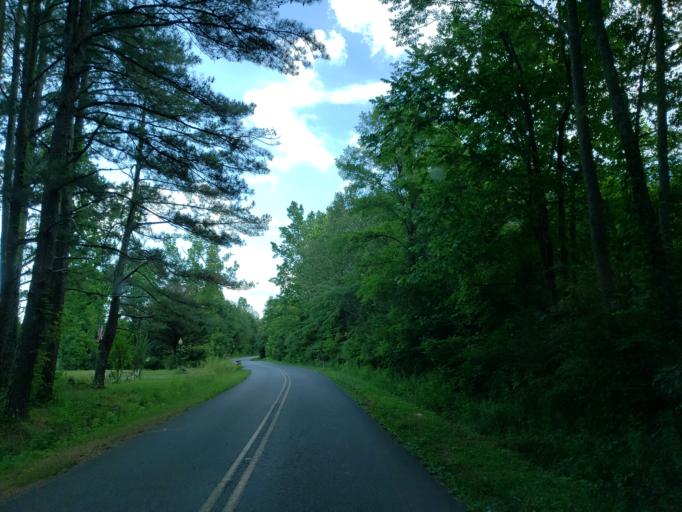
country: US
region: Georgia
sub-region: Polk County
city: Cedartown
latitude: 33.9328
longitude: -85.2711
